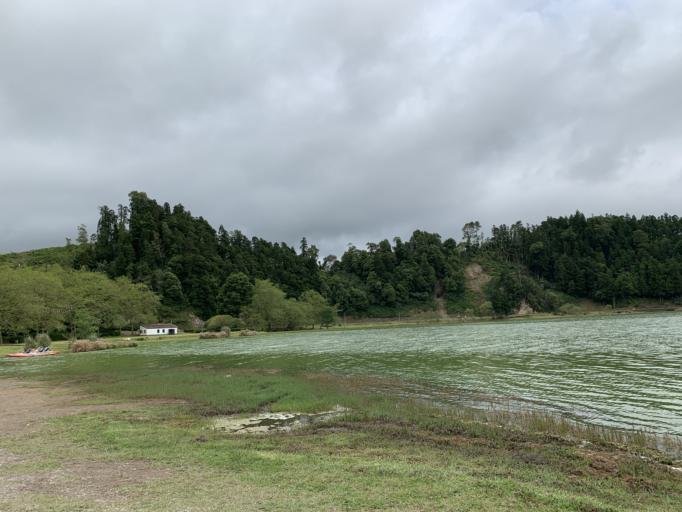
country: PT
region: Azores
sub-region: Povoacao
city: Furnas
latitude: 37.7674
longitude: -25.3310
